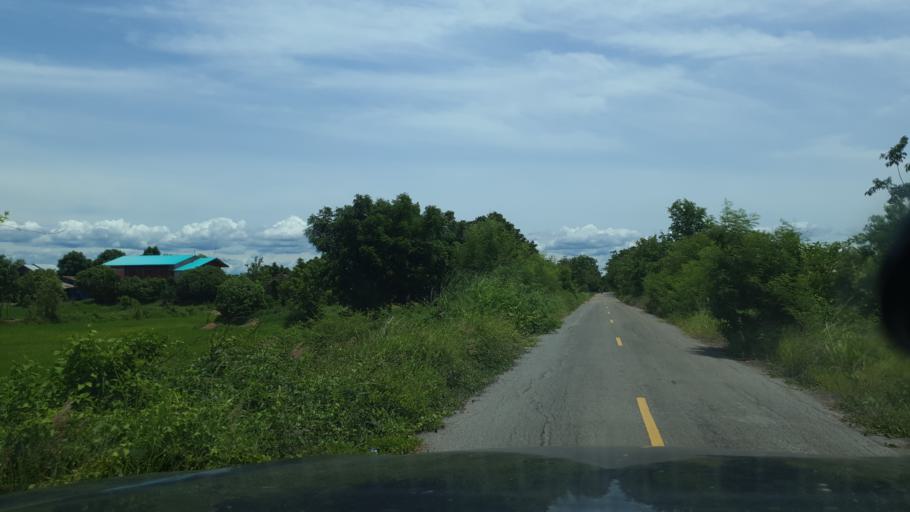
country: TH
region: Sukhothai
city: Ban Na
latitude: 17.1049
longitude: 99.6787
